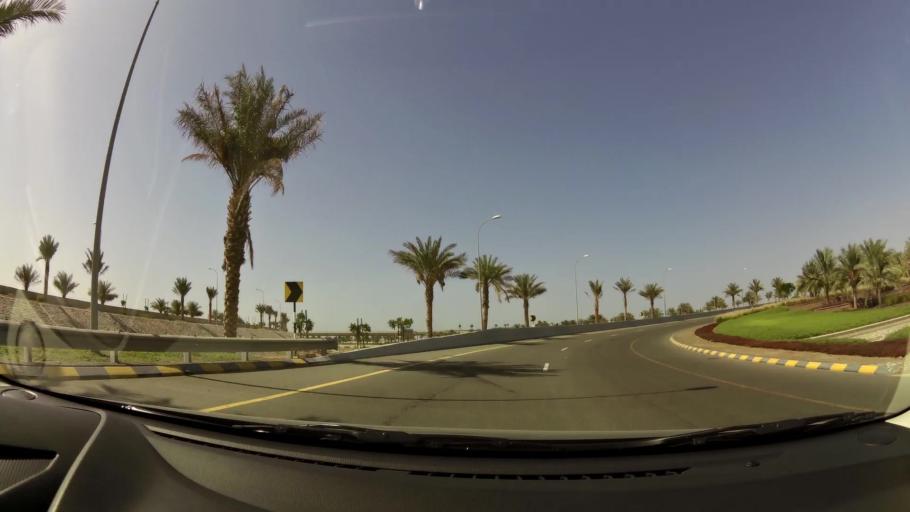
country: OM
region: Muhafazat Masqat
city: Bawshar
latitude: 23.5945
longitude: 58.3296
